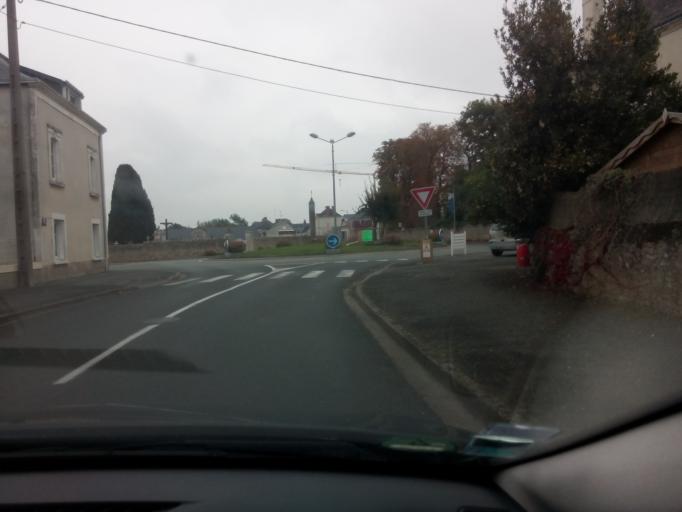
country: FR
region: Pays de la Loire
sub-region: Departement de Maine-et-Loire
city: Tierce
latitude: 47.6206
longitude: -0.5123
